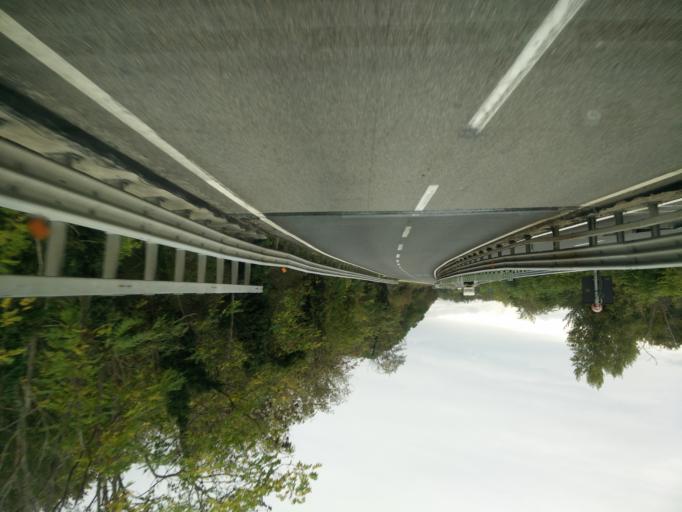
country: IT
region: Tuscany
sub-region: Province of Florence
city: Barberino Val d'Elsa
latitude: 43.5159
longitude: 11.1969
